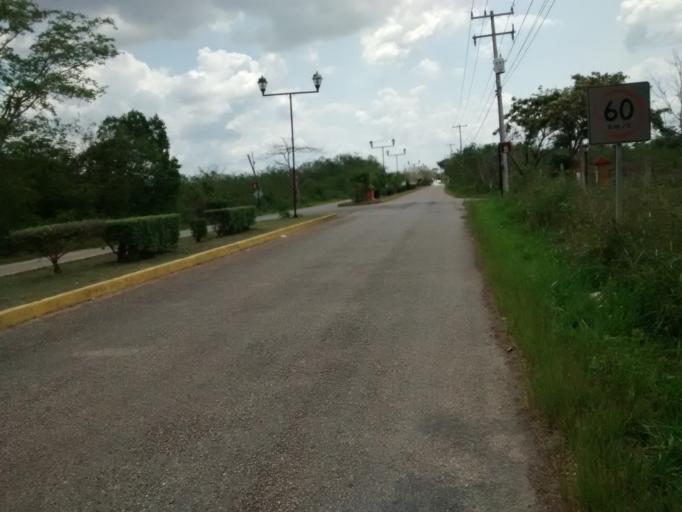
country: MX
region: Yucatan
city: Valladolid
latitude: 20.6870
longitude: -88.2228
